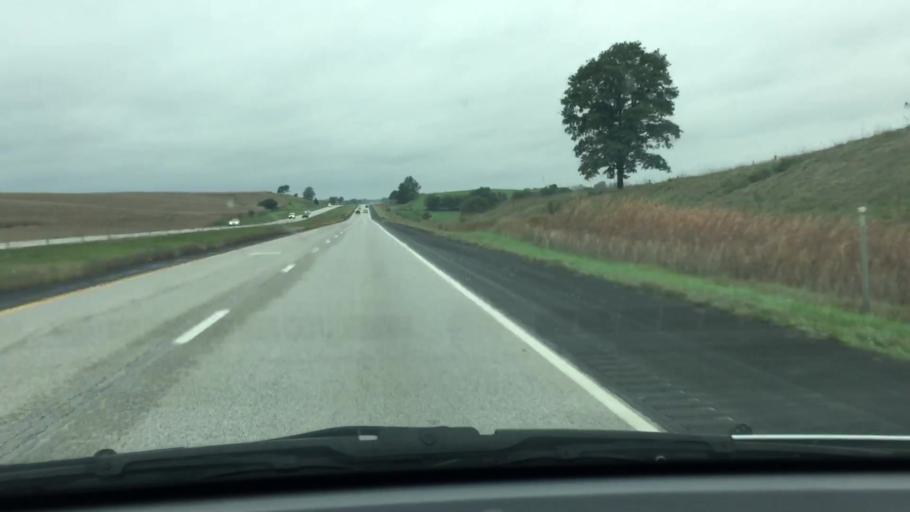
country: US
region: Iowa
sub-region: Iowa County
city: Williamsburg
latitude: 41.6874
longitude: -91.8724
